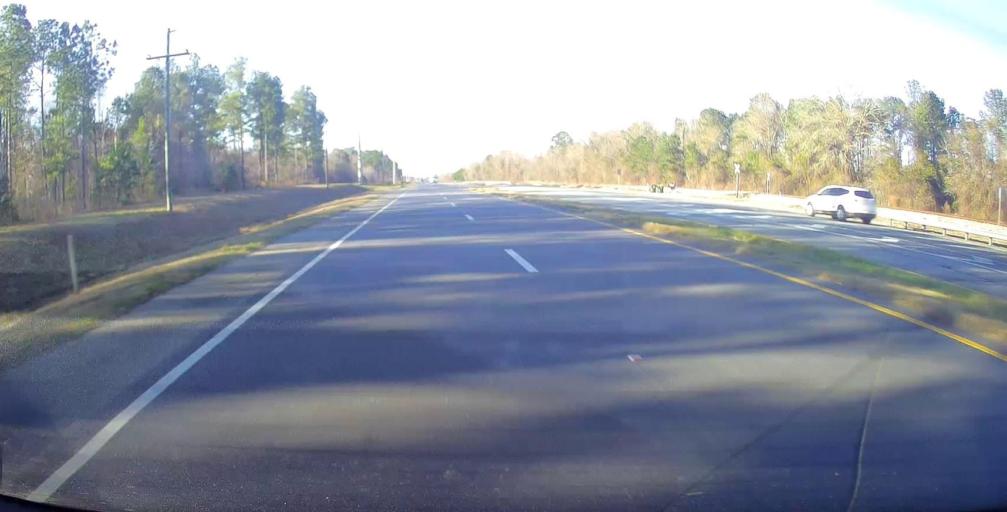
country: US
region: Georgia
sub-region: Lee County
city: Leesburg
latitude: 31.8658
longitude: -84.2357
